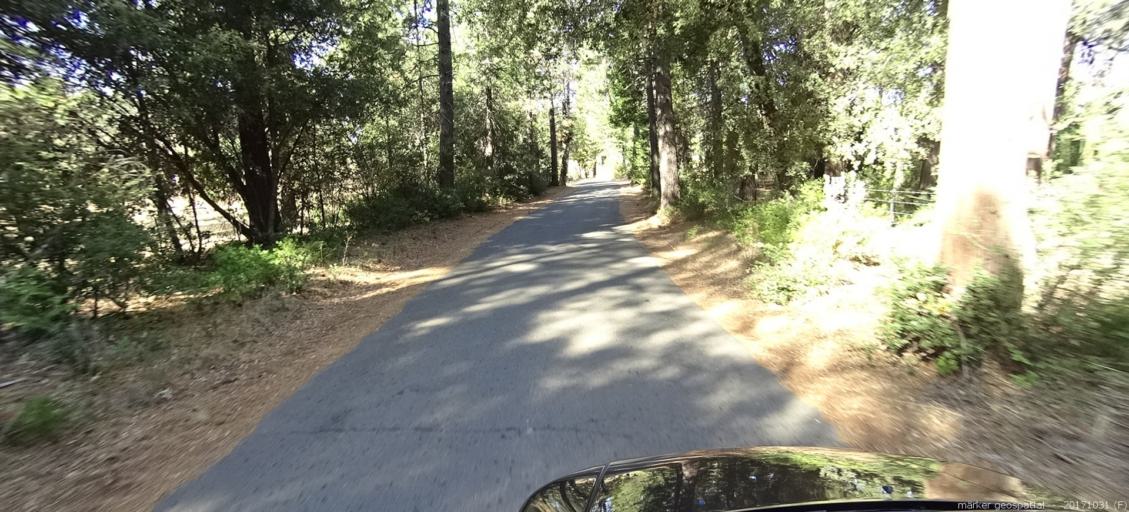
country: US
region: California
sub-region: Shasta County
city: Shingletown
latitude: 40.5341
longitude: -121.9315
